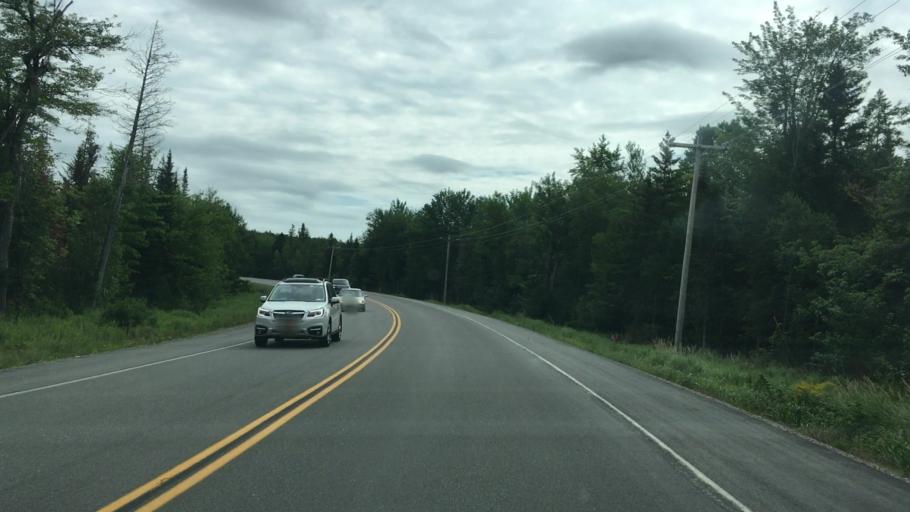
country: US
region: Maine
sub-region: Washington County
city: Machias
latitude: 44.9985
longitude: -67.5672
